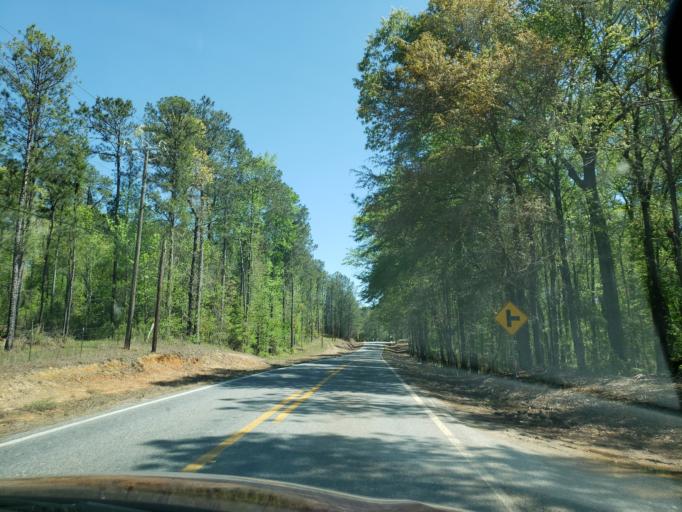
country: US
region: Alabama
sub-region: Elmore County
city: Tallassee
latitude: 32.6856
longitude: -85.8684
